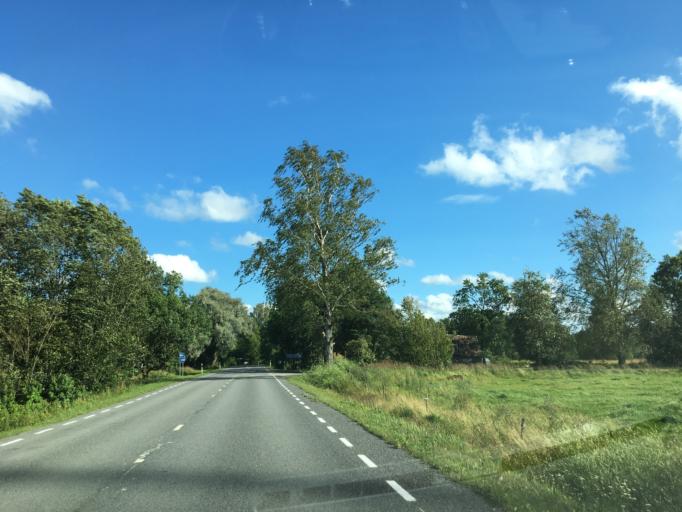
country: EE
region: Paernumaa
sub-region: Vaendra vald (alev)
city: Vandra
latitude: 58.5757
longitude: 25.1949
